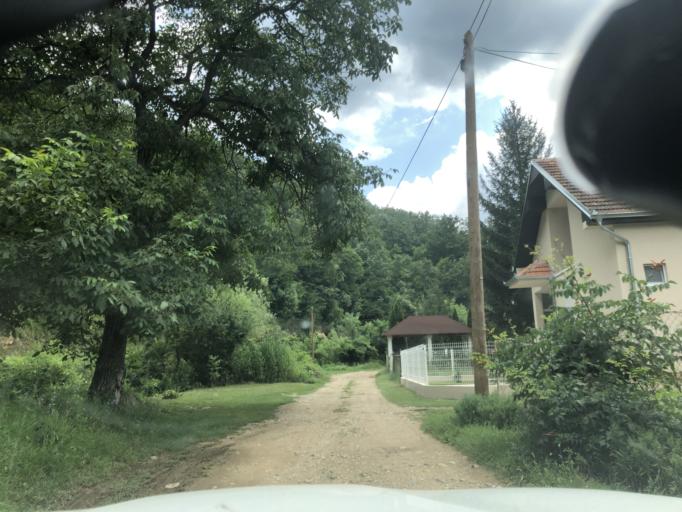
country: RS
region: Central Serbia
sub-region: Jablanicki Okrug
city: Medvega
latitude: 42.7877
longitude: 21.5861
